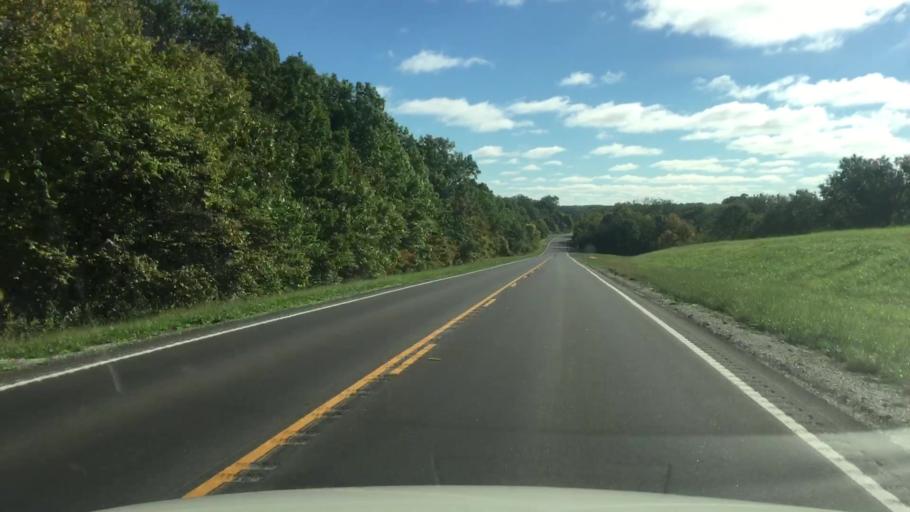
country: US
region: Missouri
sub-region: Howard County
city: New Franklin
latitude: 38.9974
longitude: -92.5891
